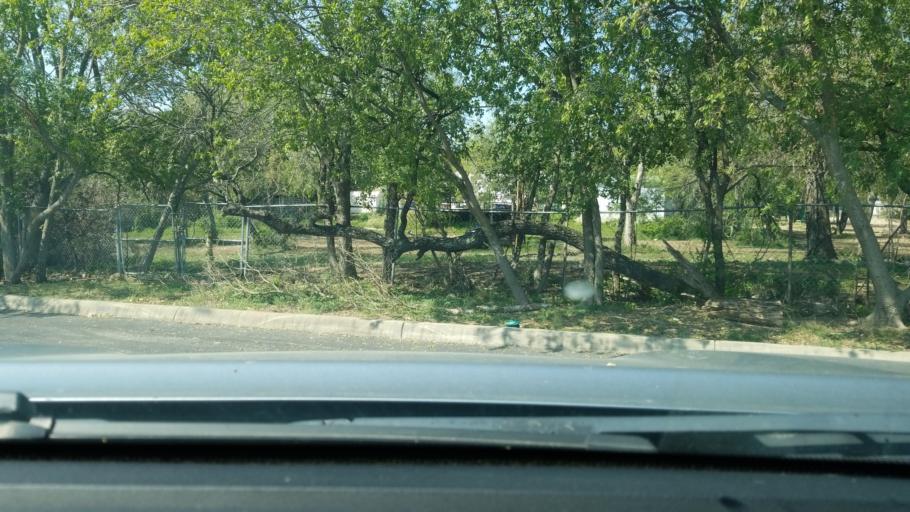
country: US
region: Texas
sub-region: Bexar County
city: Leon Valley
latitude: 29.5472
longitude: -98.6134
